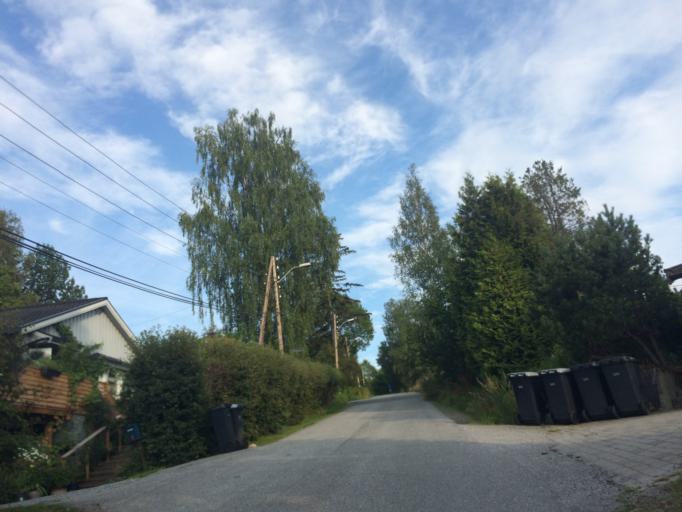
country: NO
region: Akershus
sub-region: Ski
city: Ski
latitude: 59.7089
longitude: 10.8401
